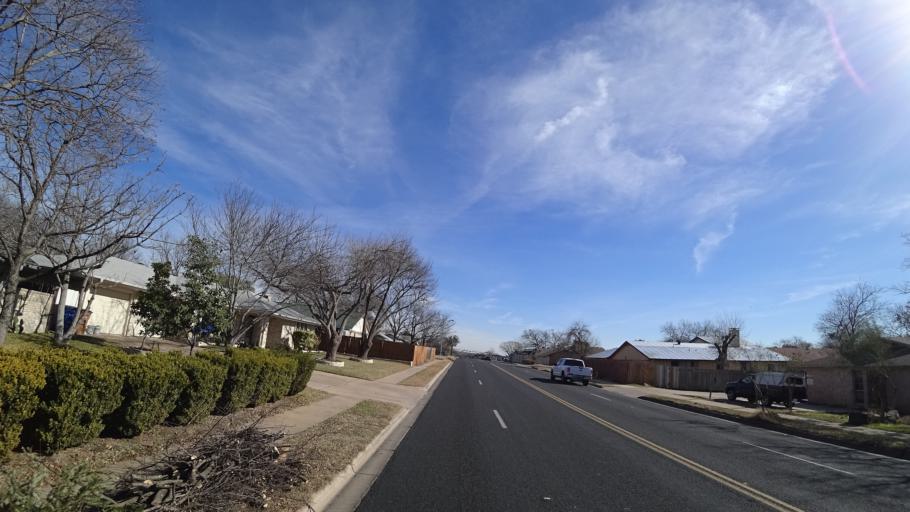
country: US
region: Texas
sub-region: Travis County
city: Wells Branch
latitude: 30.3703
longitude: -97.7076
